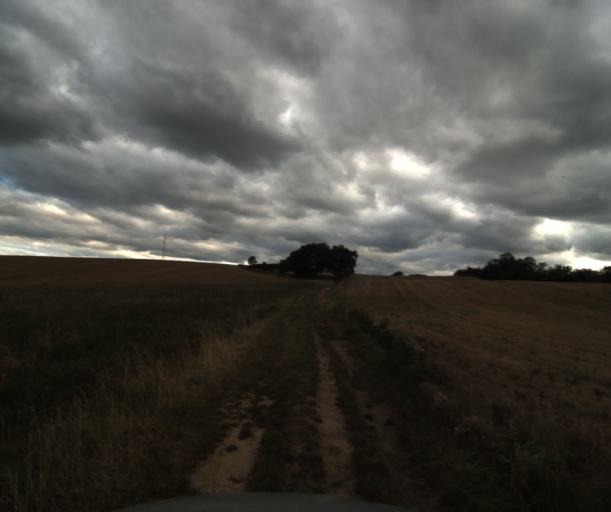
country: FR
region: Midi-Pyrenees
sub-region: Departement de la Haute-Garonne
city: Le Fauga
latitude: 43.3954
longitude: 1.3099
